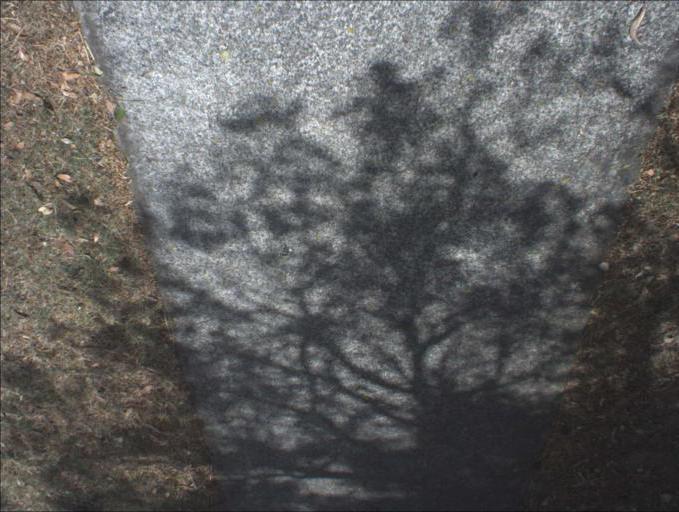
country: AU
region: Queensland
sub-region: Logan
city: Slacks Creek
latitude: -27.6572
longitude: 153.1750
